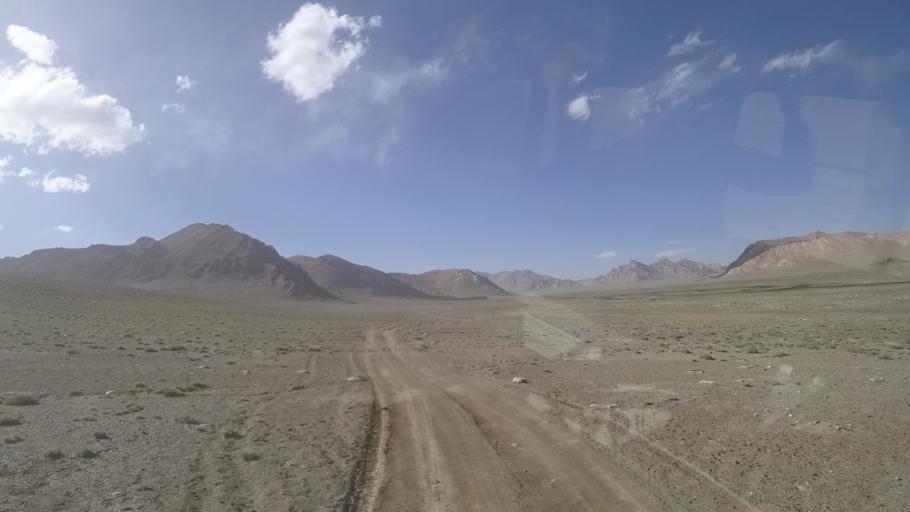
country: TJ
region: Gorno-Badakhshan
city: Murghob
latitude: 37.5843
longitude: 74.1547
